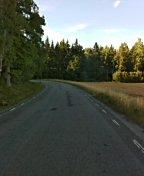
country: SE
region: Uppsala
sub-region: Habo Kommun
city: Balsta
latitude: 59.6876
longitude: 17.5353
